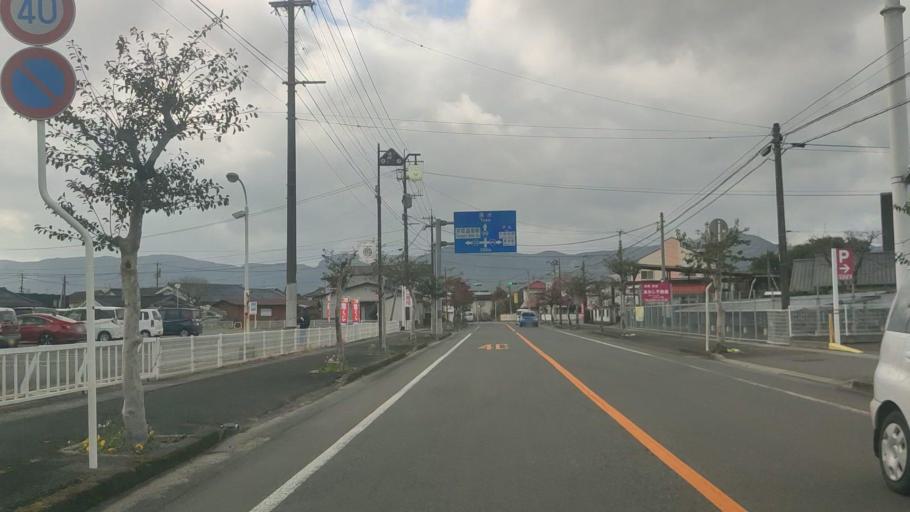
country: JP
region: Kagoshima
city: Okuchi-shinohara
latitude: 32.0480
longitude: 130.7687
